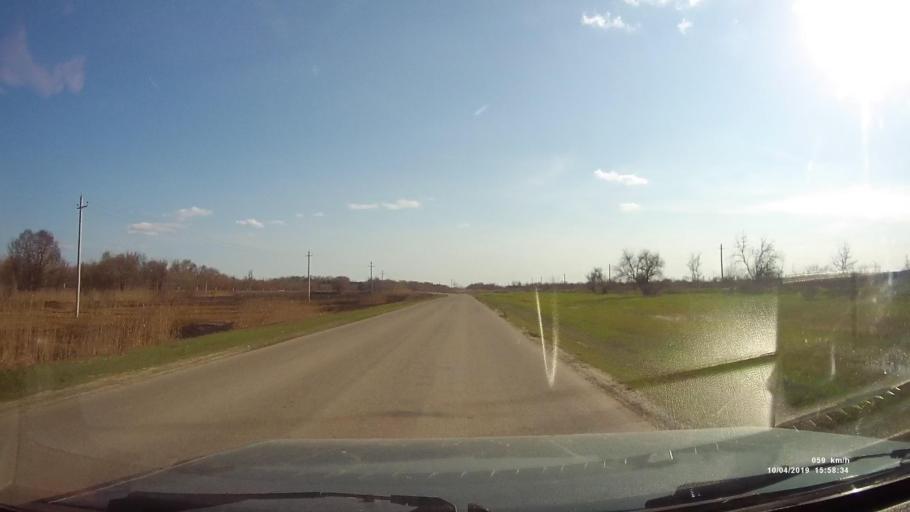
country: RU
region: Rostov
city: Masalovka
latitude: 48.4018
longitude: 40.2716
